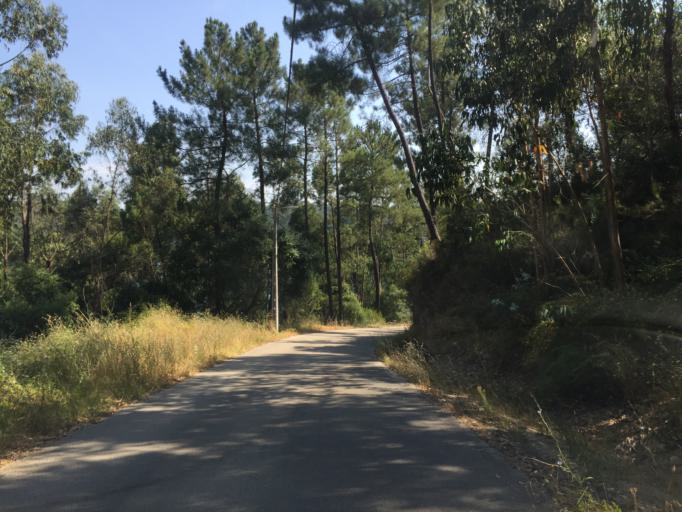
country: PT
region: Santarem
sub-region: Ferreira do Zezere
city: Ferreira do Zezere
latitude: 39.6085
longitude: -8.2820
